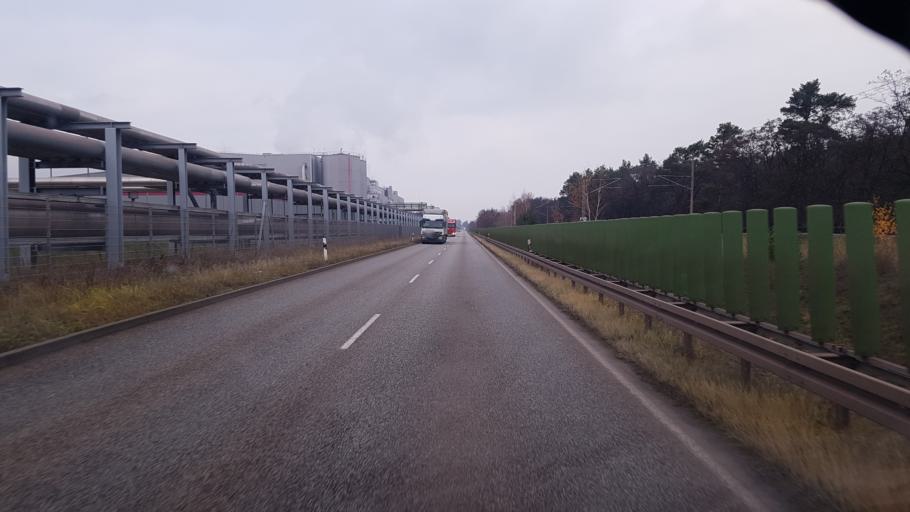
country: DE
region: Brandenburg
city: Vogelsang
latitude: 52.1760
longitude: 14.6396
